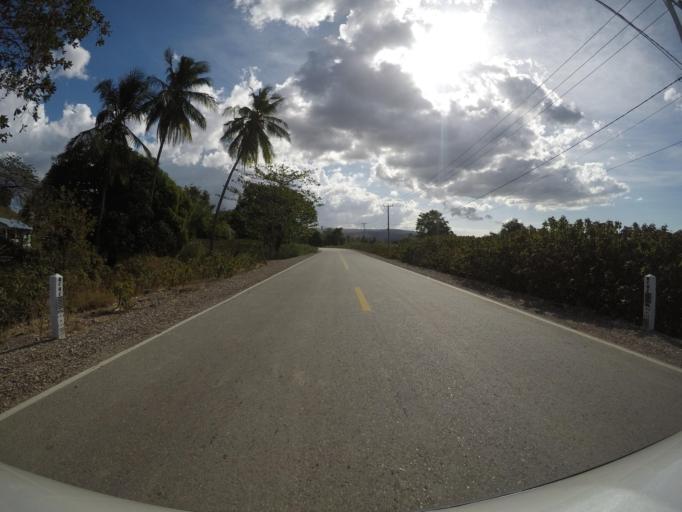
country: TL
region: Baucau
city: Baucau
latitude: -8.4759
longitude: 126.5327
